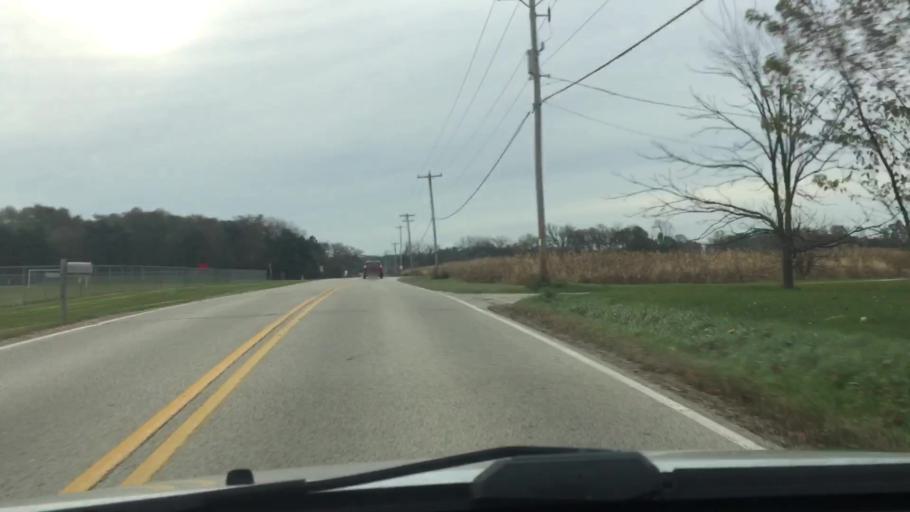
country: US
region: Wisconsin
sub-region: Waukesha County
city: North Prairie
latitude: 42.8915
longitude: -88.3826
